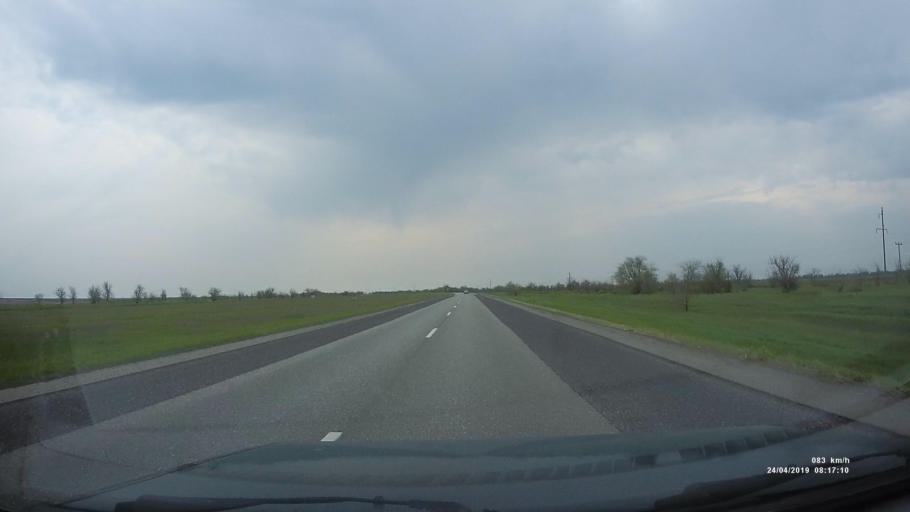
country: RU
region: Kalmykiya
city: Priyutnoye
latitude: 46.0982
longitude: 43.6251
